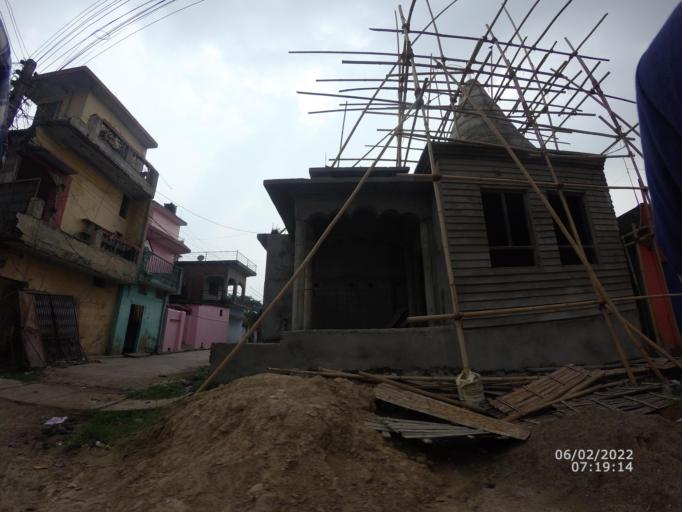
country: NP
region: Western Region
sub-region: Lumbini Zone
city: Bhairahawa
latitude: 27.4854
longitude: 83.4387
